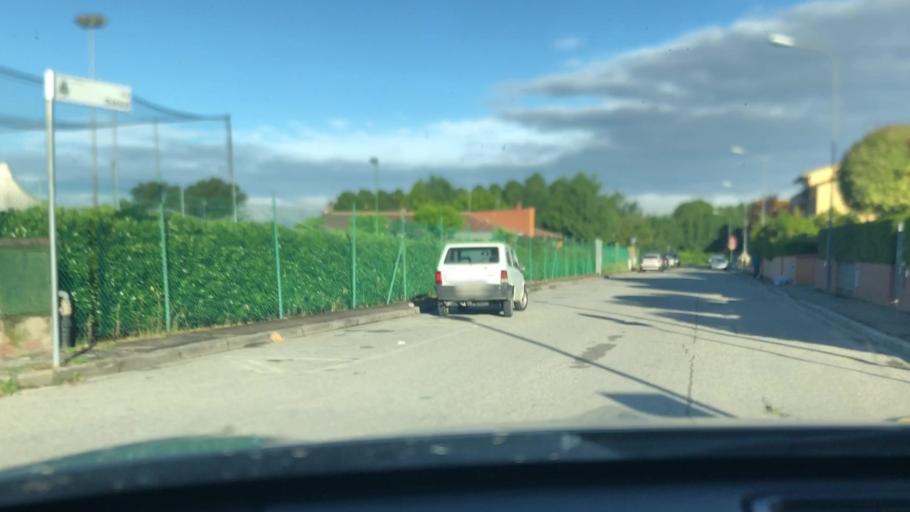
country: IT
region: Tuscany
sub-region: Province of Pisa
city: Forcoli
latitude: 43.6024
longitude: 10.7056
